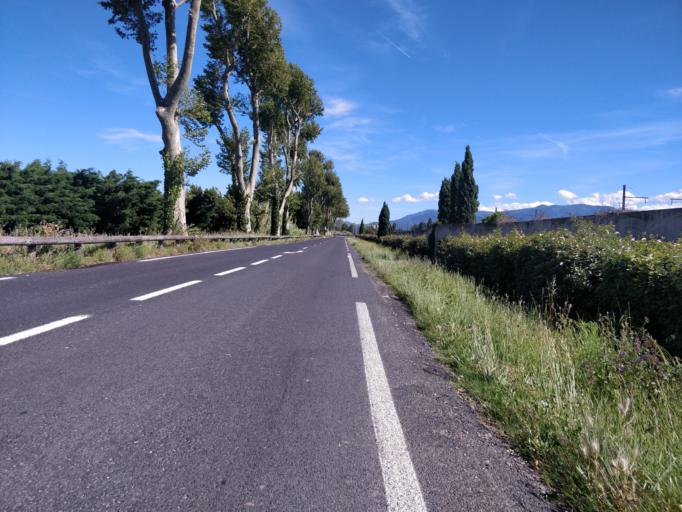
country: FR
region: Languedoc-Roussillon
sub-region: Departement des Pyrenees-Orientales
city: Corneilla-del-Vercol
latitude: 42.6210
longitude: 2.9522
